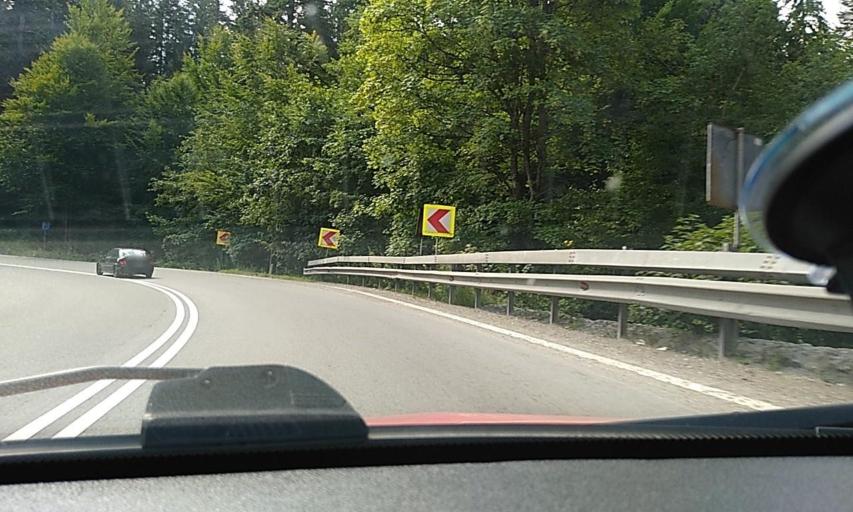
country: RO
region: Brasov
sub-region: Oras Predeal
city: Predeal
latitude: 45.5267
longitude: 25.5774
